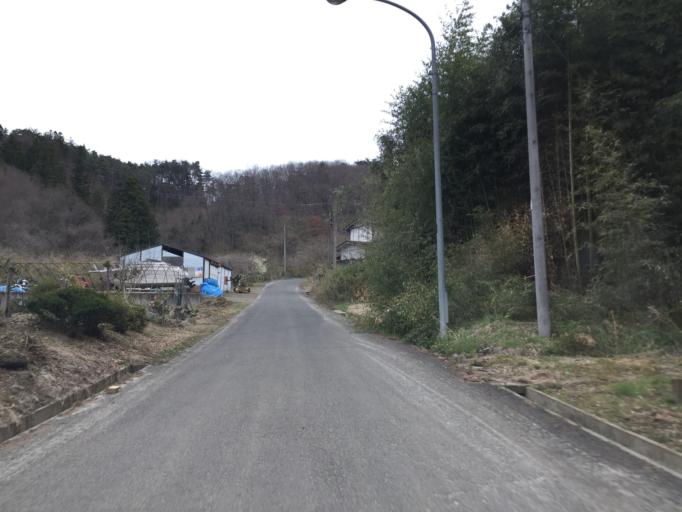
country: JP
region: Fukushima
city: Fukushima-shi
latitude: 37.7231
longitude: 140.4194
